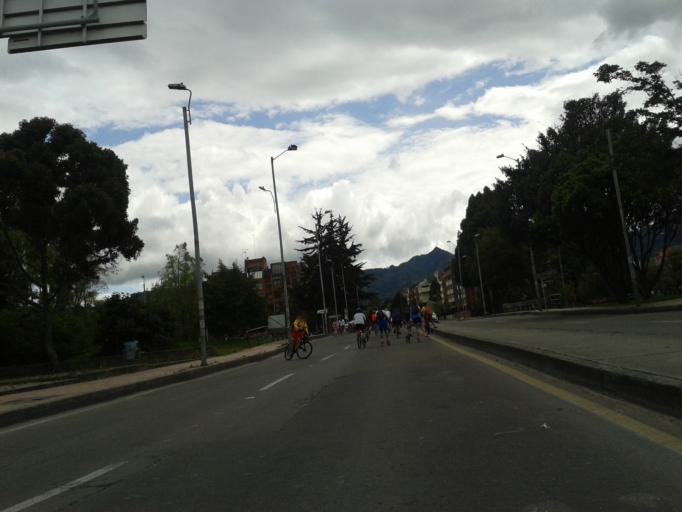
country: CO
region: Bogota D.C.
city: Barrio San Luis
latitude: 4.7016
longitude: -74.0667
